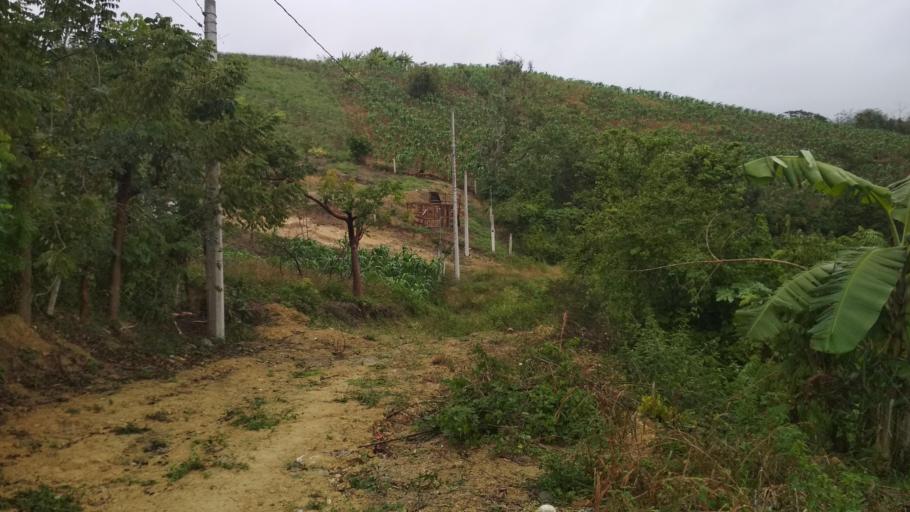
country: MX
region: Veracruz
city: Papantla de Olarte
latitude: 20.4656
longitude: -97.3092
